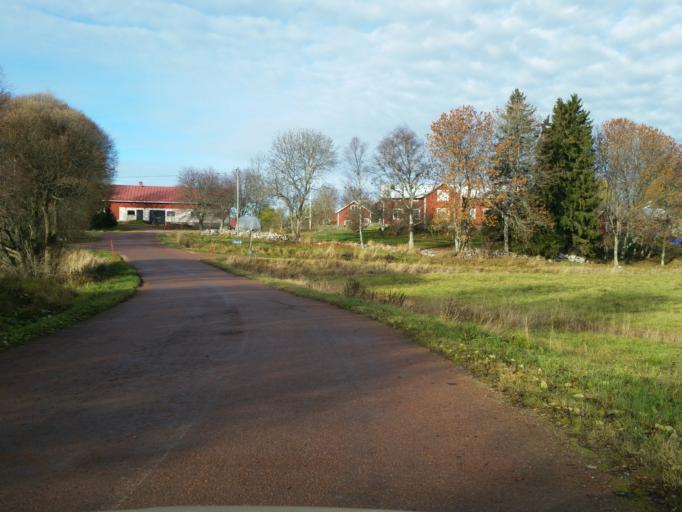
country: AX
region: Alands skaergard
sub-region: Kumlinge
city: Kumlinge
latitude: 60.2608
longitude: 20.7782
